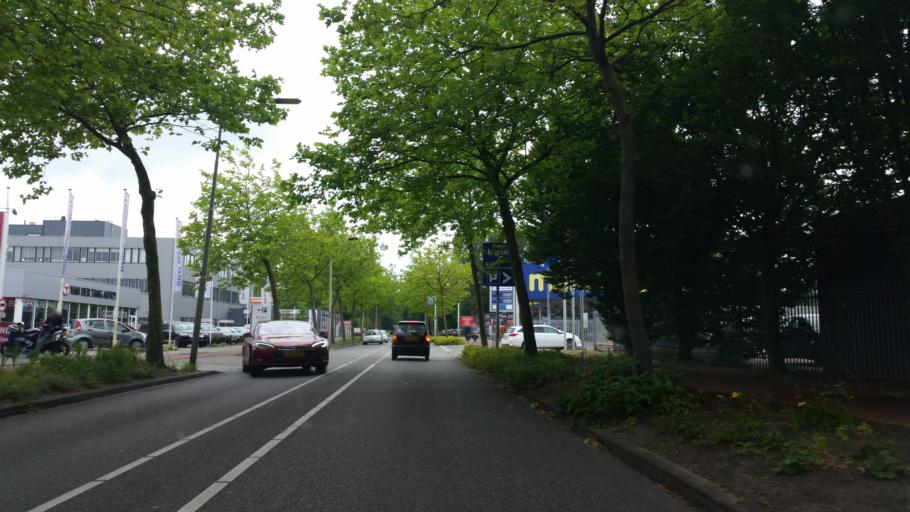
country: NL
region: South Holland
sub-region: Gemeente Delft
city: Delft
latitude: 51.9834
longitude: 4.3718
